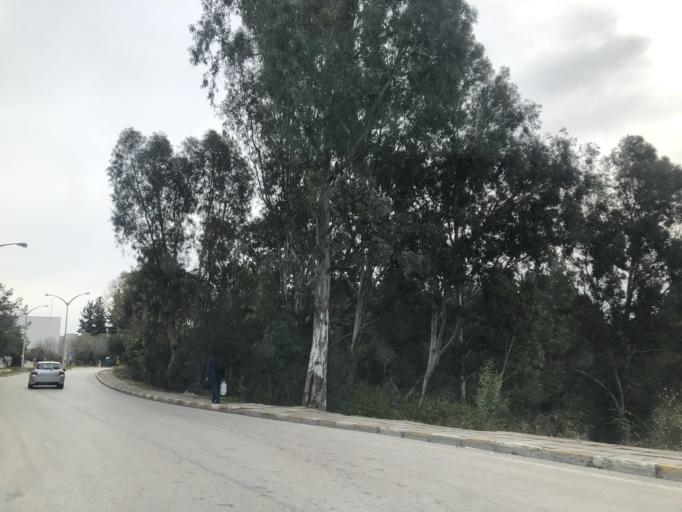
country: TR
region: Adana
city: Adana
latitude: 37.0577
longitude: 35.3528
